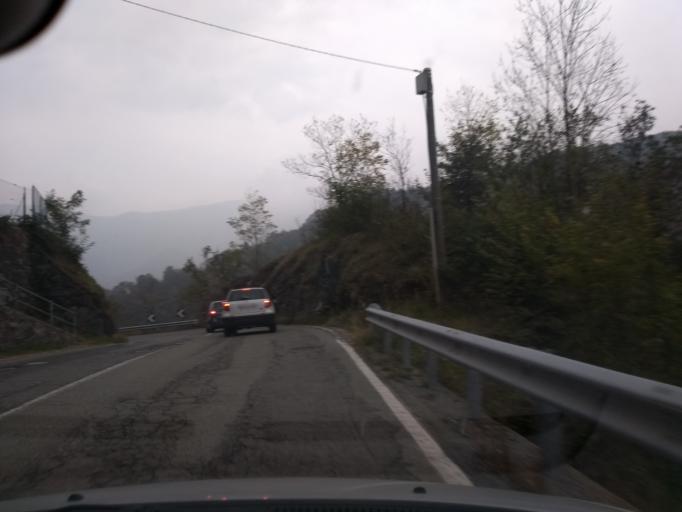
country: IT
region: Piedmont
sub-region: Provincia di Torino
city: La Villa
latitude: 45.2712
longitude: 7.4472
